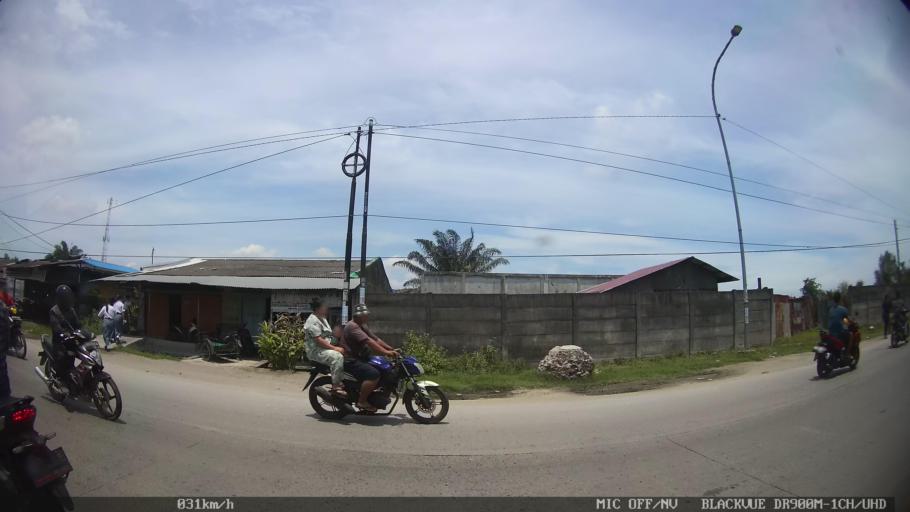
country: ID
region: North Sumatra
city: Belawan
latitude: 3.7583
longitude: 98.6792
